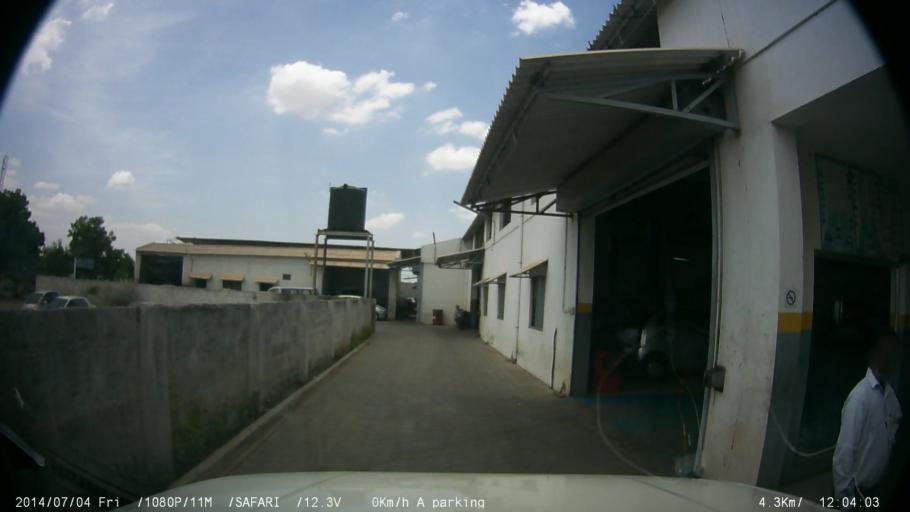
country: IN
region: Tamil Nadu
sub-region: Tiruppur
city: Tiruppur
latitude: 11.0741
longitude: 77.3411
